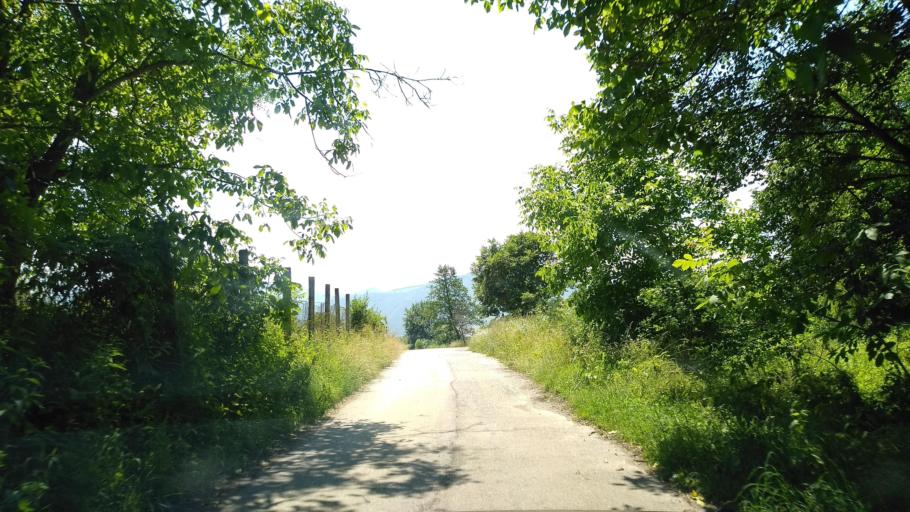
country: RO
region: Hunedoara
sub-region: Comuna Sarmizegetusa
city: Sarmizegetusa
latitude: 45.5429
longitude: 22.8183
